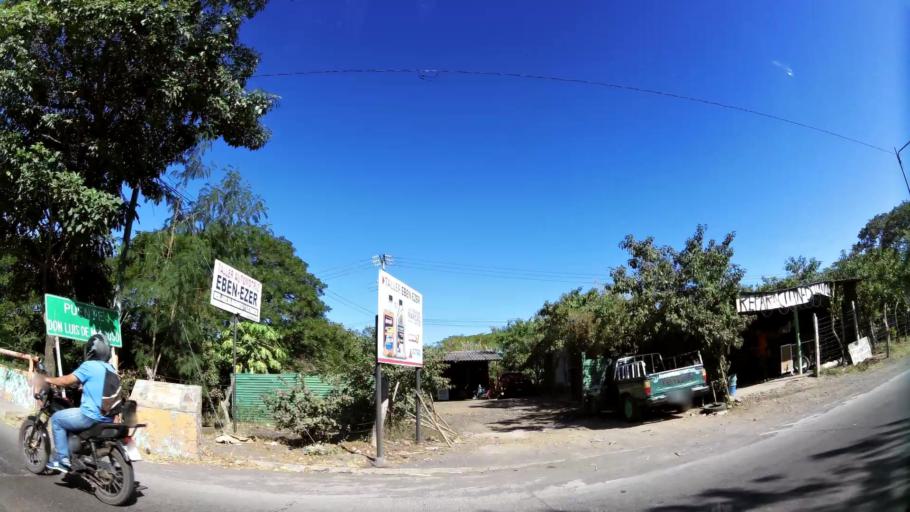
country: SV
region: San Miguel
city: San Miguel
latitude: 13.4605
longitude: -88.1514
